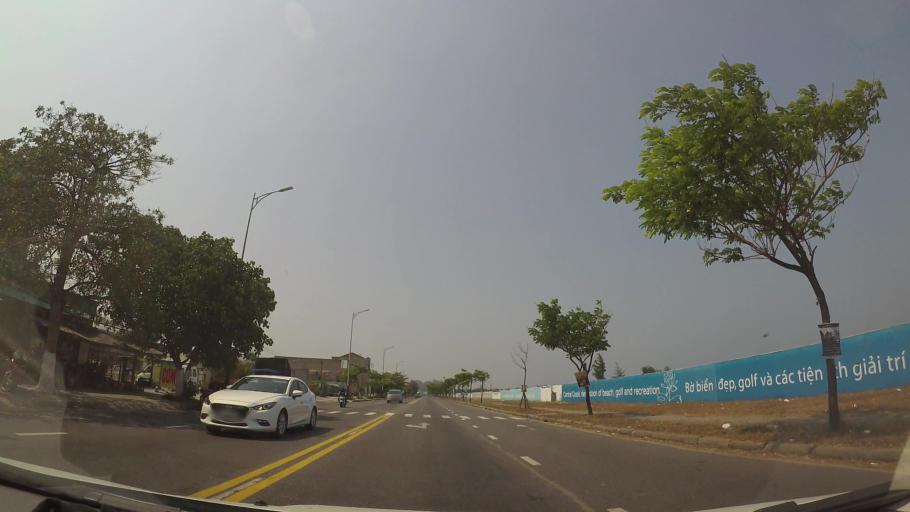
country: VN
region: Da Nang
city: Ngu Hanh Son
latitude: 15.9823
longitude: 108.2752
